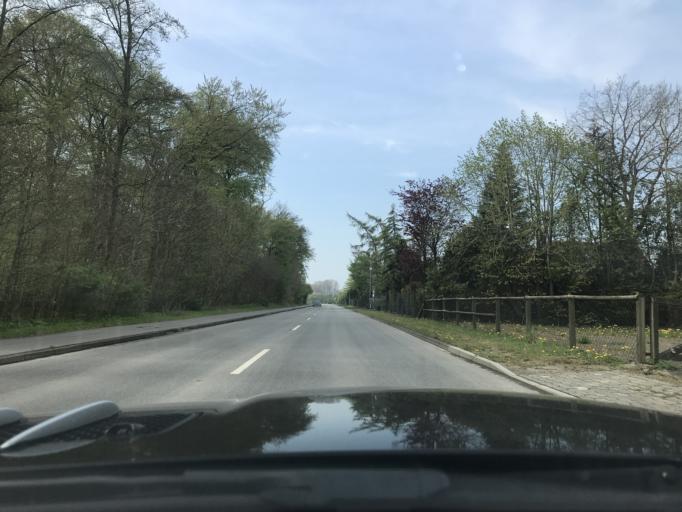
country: DE
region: Schleswig-Holstein
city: Kellenhusen
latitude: 54.2048
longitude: 11.0355
